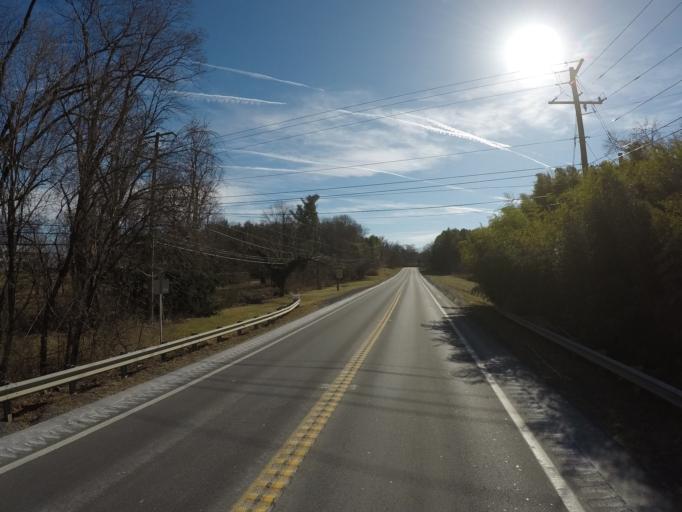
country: US
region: Virginia
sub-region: Loudoun County
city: Leesburg
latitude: 39.1676
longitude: -77.5362
